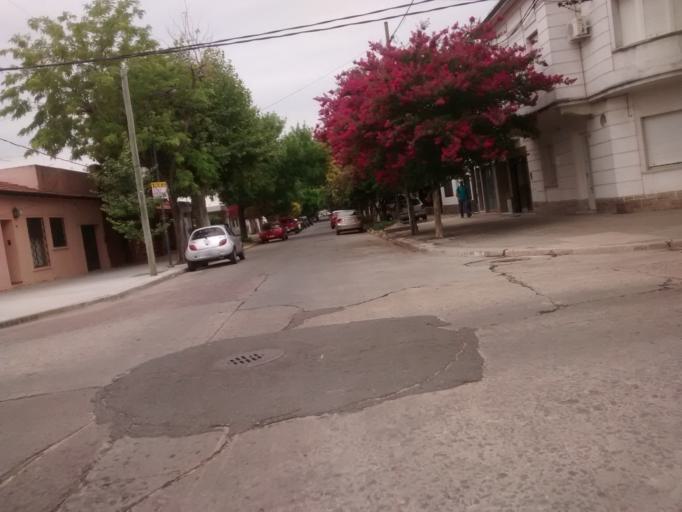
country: AR
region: Buenos Aires
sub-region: Partido de La Plata
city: La Plata
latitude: -34.9012
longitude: -57.9635
